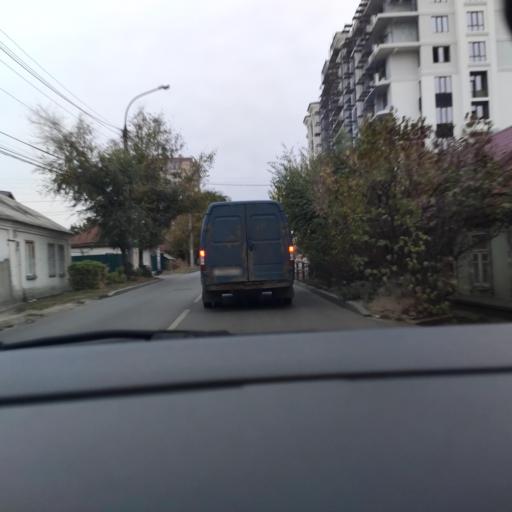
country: RU
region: Voronezj
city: Voronezh
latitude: 51.6445
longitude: 39.1763
